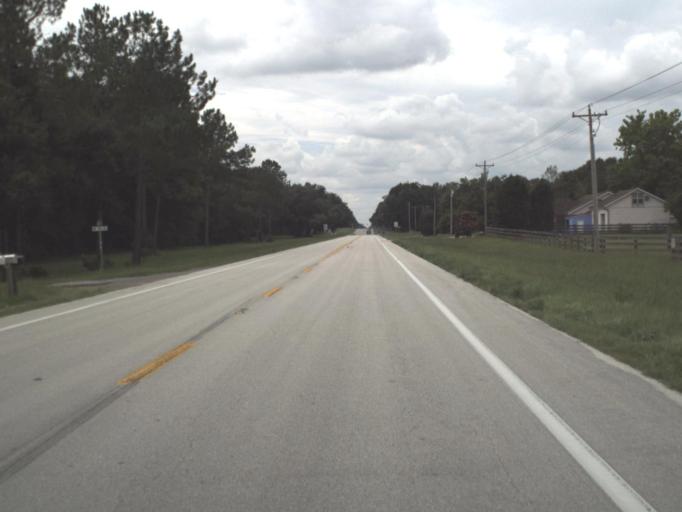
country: US
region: Florida
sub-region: Alachua County
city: Newberry
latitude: 29.7335
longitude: -82.6072
